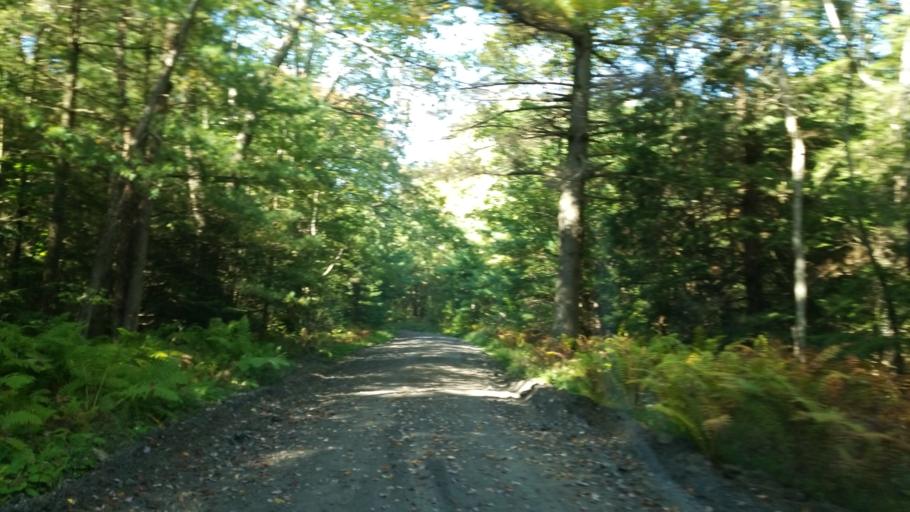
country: US
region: Pennsylvania
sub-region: Clearfield County
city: Curwensville
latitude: 41.1137
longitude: -78.5657
